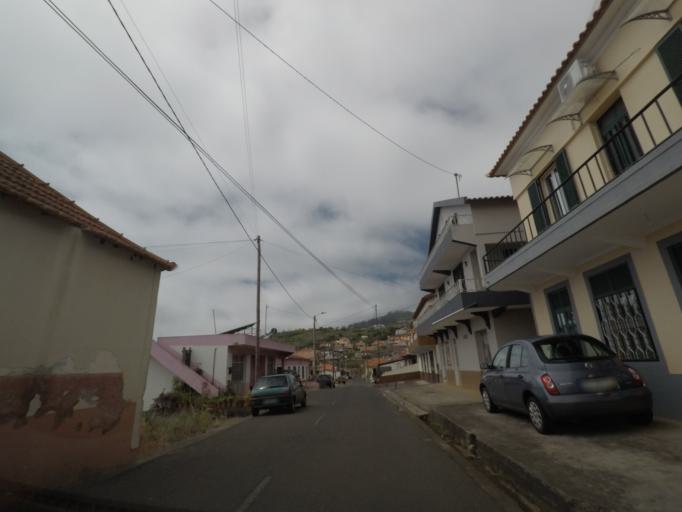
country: PT
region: Madeira
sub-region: Calheta
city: Arco da Calheta
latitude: 32.7127
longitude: -17.1214
